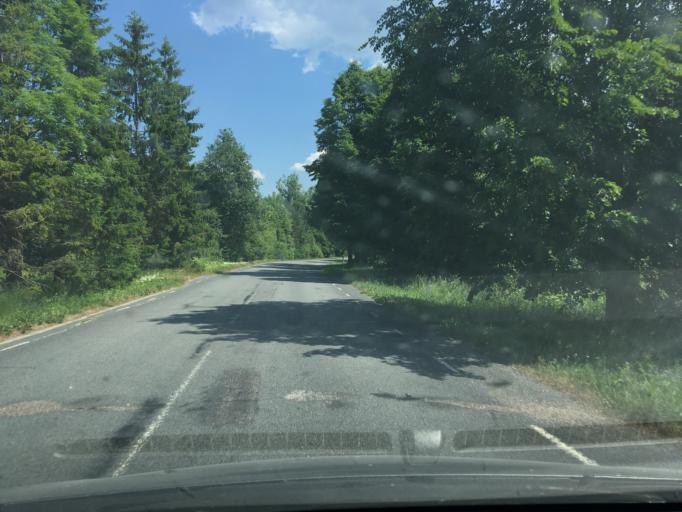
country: EE
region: Paernumaa
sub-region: Halinga vald
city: Parnu-Jaagupi
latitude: 58.7175
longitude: 24.3526
